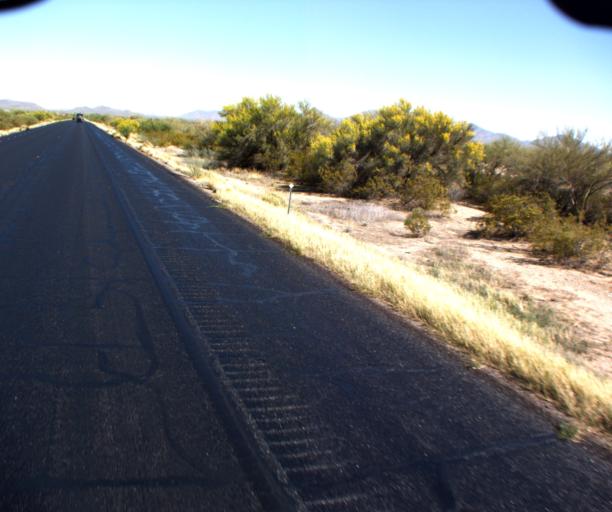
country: US
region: Arizona
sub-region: Pinal County
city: Maricopa
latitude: 32.8440
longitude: -112.2726
